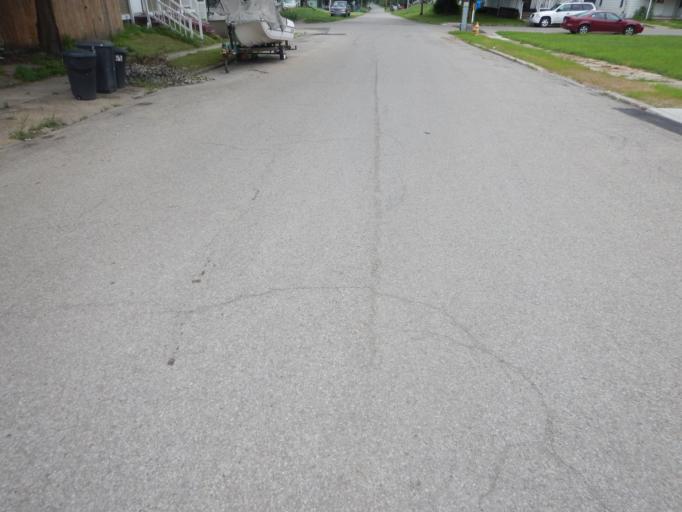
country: US
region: Ohio
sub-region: Muskingum County
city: Zanesville
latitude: 39.9339
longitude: -82.0264
